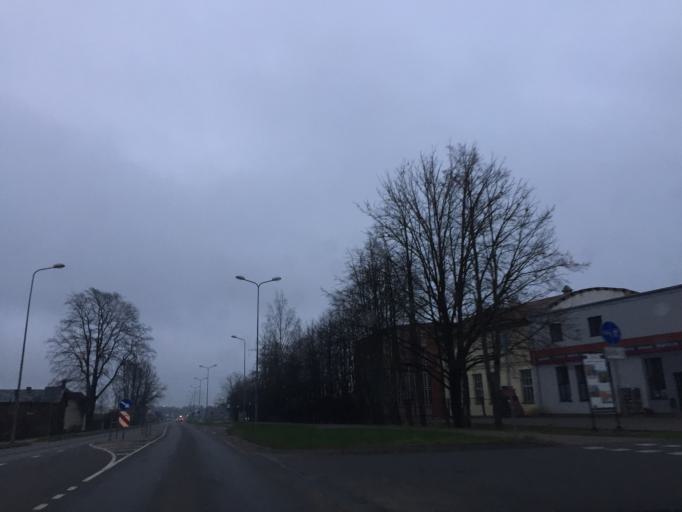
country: LV
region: Valmieras Rajons
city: Valmiera
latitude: 57.5441
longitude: 25.3918
